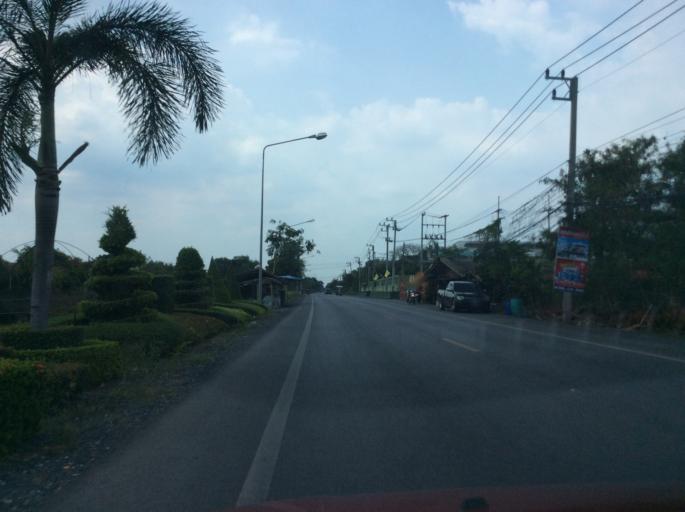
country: TH
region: Pathum Thani
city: Lam Luk Ka
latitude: 13.9522
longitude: 100.7272
